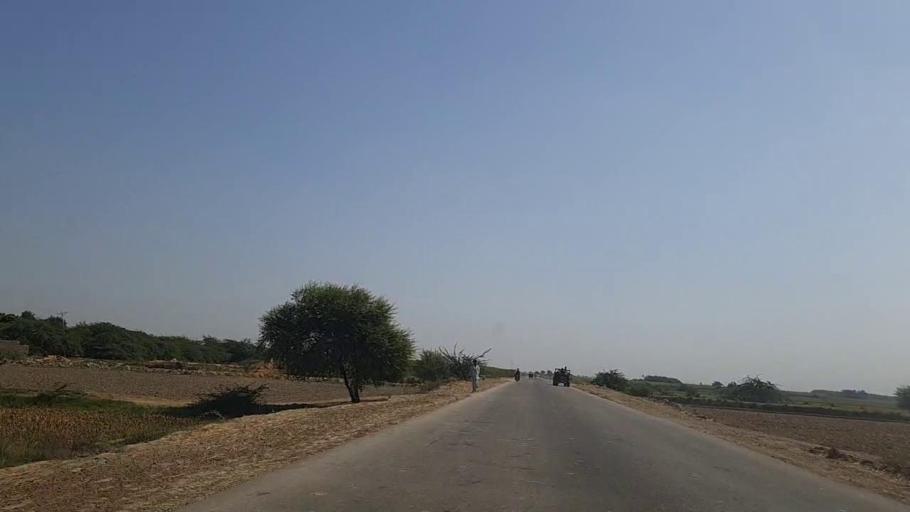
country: PK
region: Sindh
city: Mirpur Batoro
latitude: 24.7563
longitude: 68.2274
